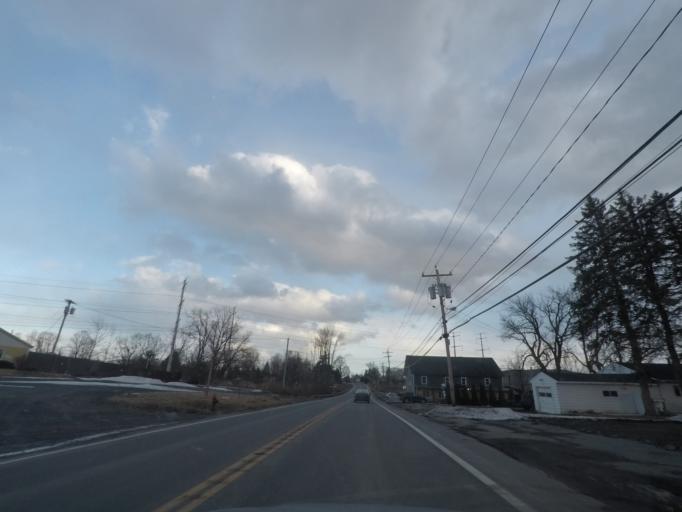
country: US
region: New York
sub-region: Oneida County
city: Utica
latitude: 43.1040
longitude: -75.1621
